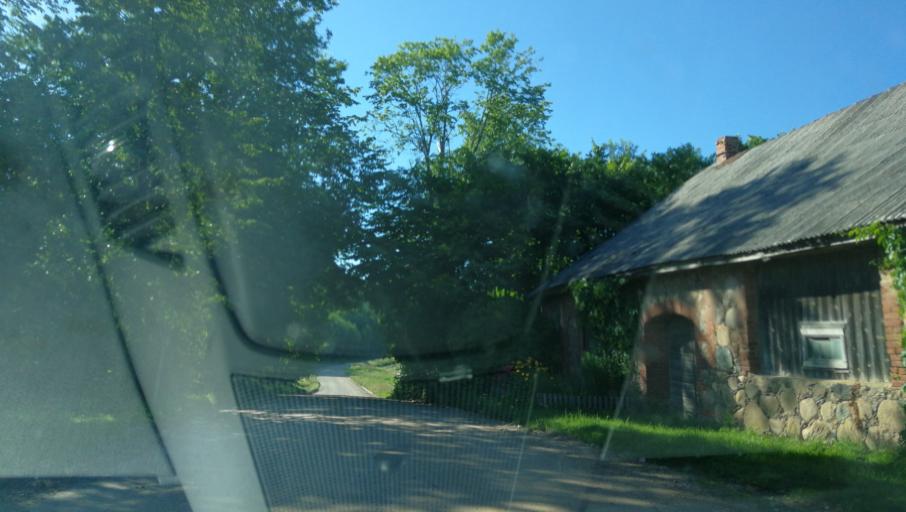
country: LV
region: Jaunpiebalga
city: Jaunpiebalga
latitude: 57.0262
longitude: 26.0258
